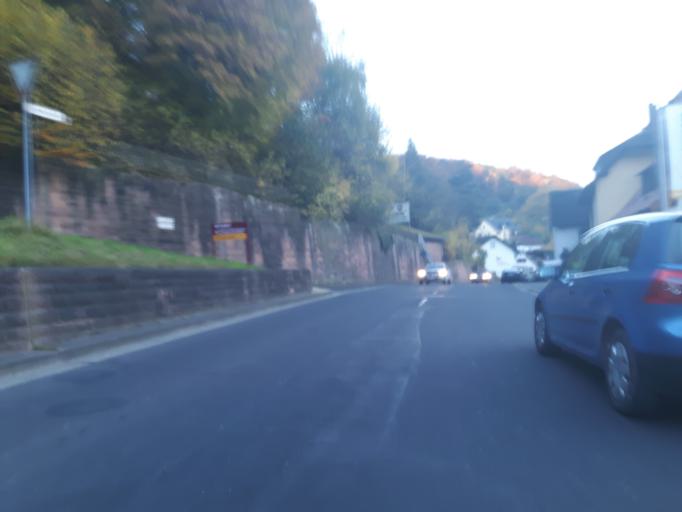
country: DE
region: Bavaria
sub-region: Regierungsbezirk Unterfranken
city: Heimbuchenthal
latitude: 49.8975
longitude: 9.3051
